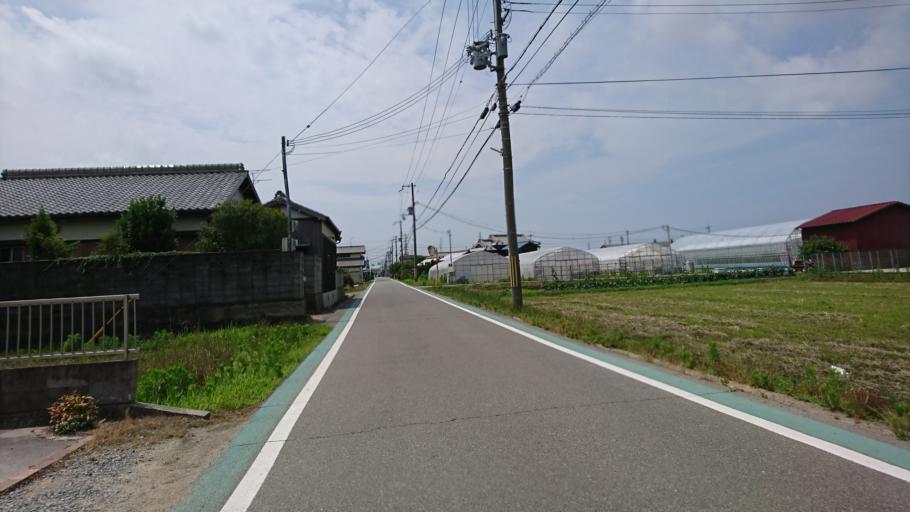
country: JP
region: Hyogo
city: Kakogawacho-honmachi
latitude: 34.7360
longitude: 134.9118
